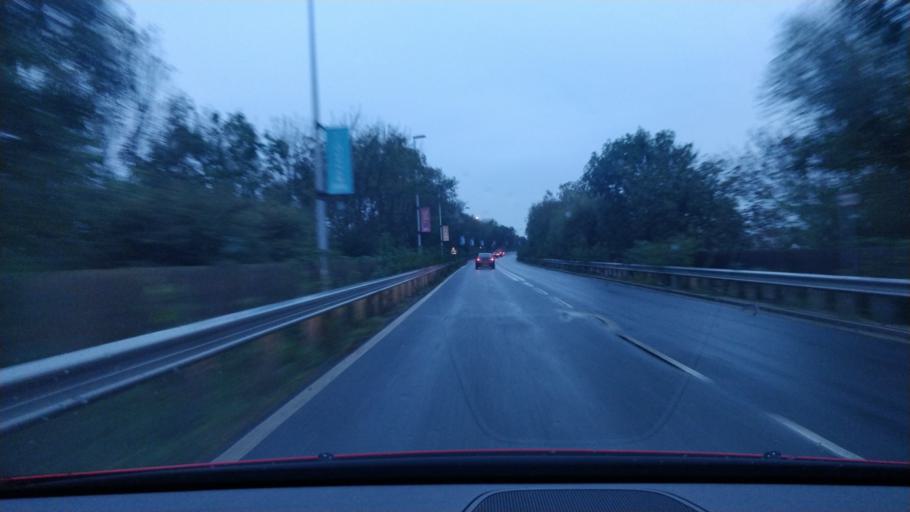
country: GB
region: England
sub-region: Lancashire
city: Great Marton
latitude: 53.7929
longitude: -3.0358
